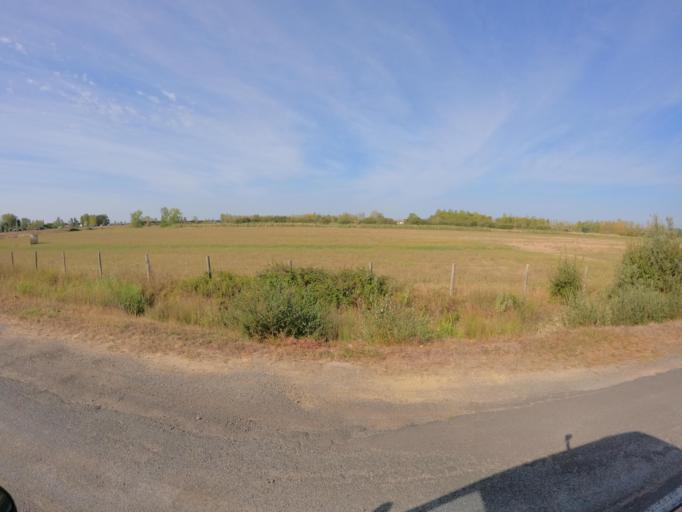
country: FR
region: Pays de la Loire
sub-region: Departement de la Vendee
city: Le Perrier
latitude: 46.8054
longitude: -1.9841
